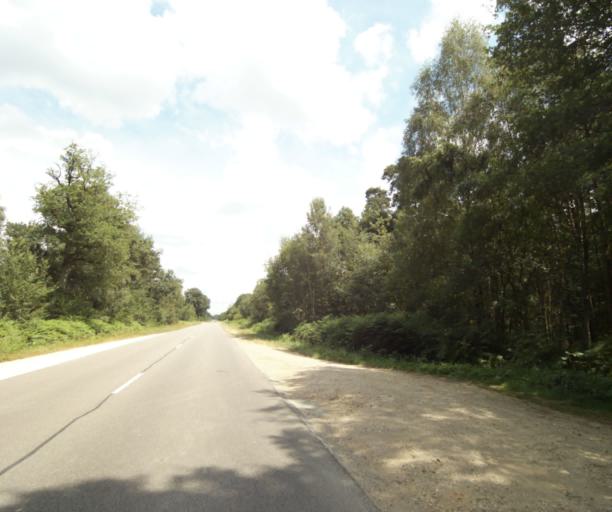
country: FR
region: Ile-de-France
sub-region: Departement de Seine-et-Marne
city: Champagne-sur-Seine
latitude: 48.4196
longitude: 2.8216
